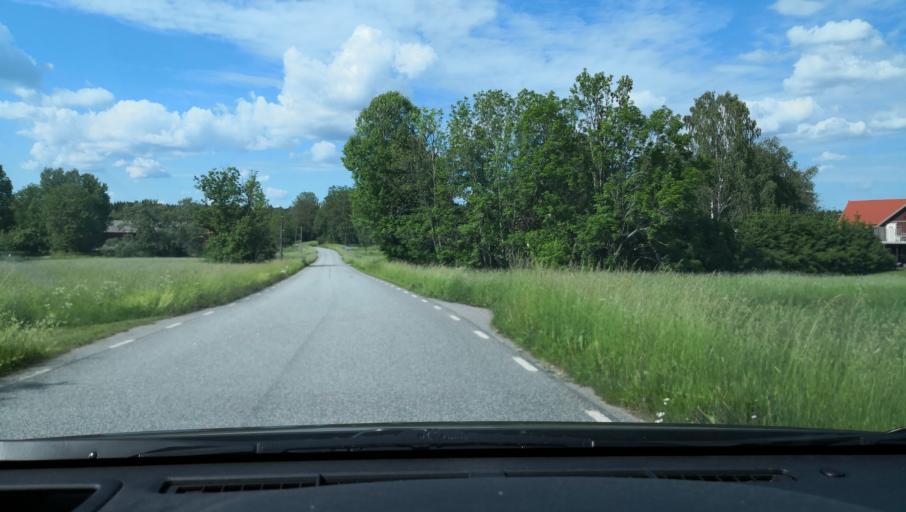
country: SE
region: Uppsala
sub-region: Enkopings Kommun
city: Orsundsbro
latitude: 59.8289
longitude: 17.3191
